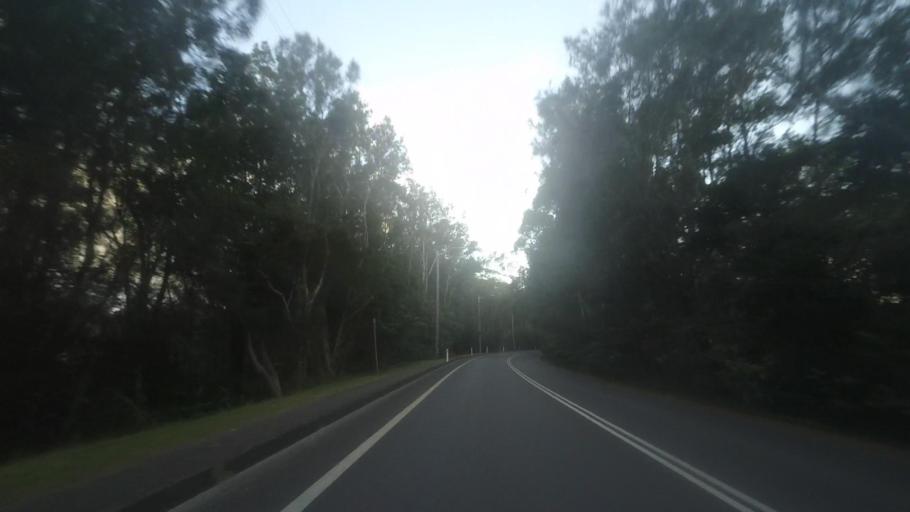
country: AU
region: New South Wales
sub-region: Great Lakes
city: Hawks Nest
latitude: -32.6673
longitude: 152.1728
